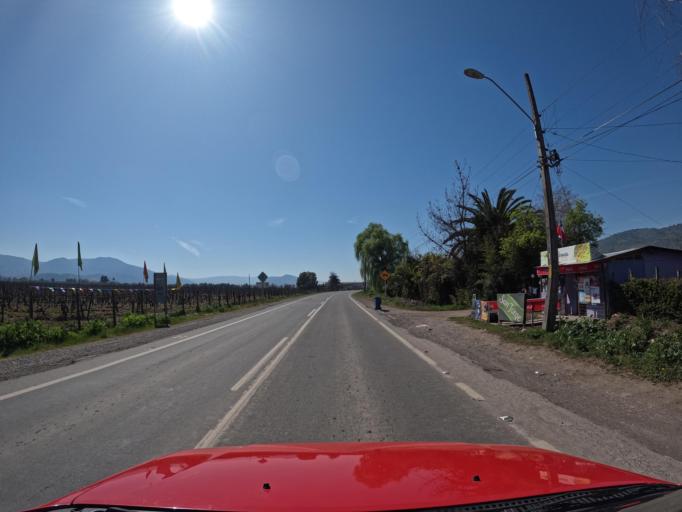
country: CL
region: Maule
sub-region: Provincia de Curico
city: Rauco
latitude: -35.0182
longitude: -71.4260
